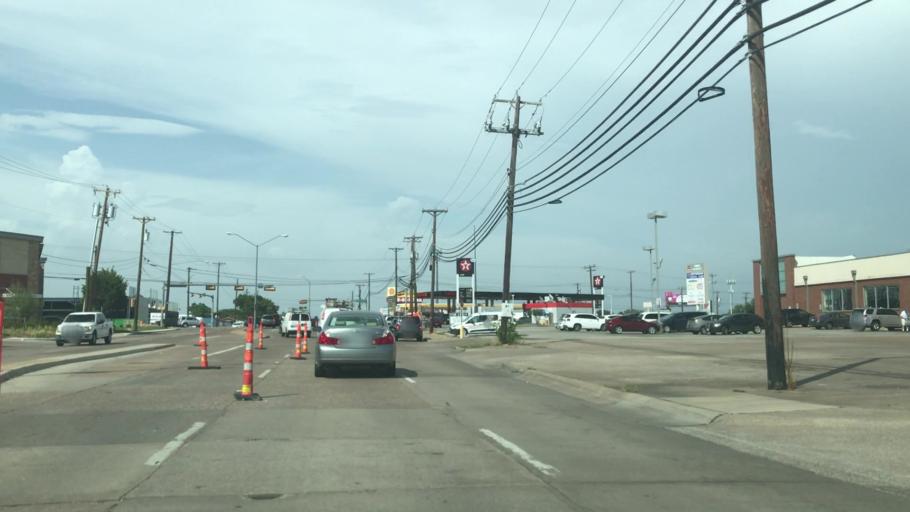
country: US
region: Texas
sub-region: Dallas County
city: Highland Park
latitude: 32.8558
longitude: -96.7508
